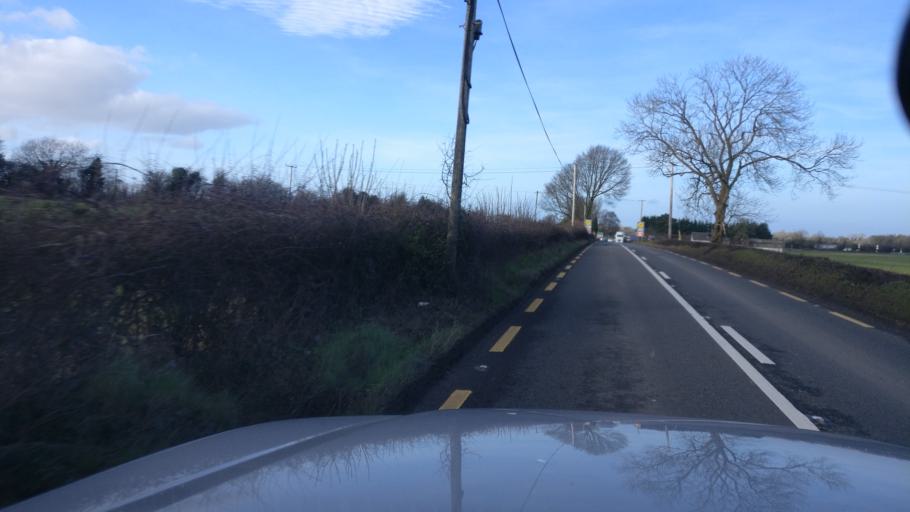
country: IE
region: Leinster
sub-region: Laois
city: Mountmellick
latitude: 53.0979
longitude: -7.3380
